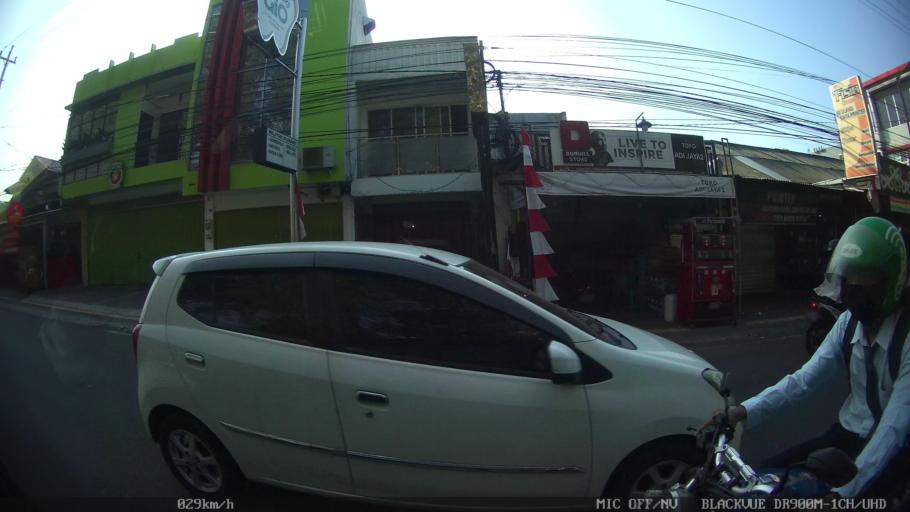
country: ID
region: Daerah Istimewa Yogyakarta
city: Depok
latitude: -7.7635
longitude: 110.4119
